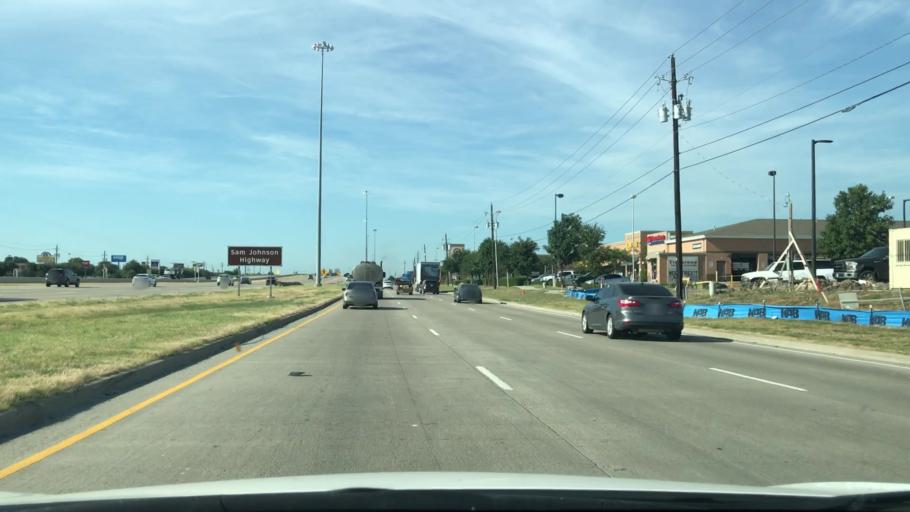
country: US
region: Texas
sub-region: Collin County
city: McKinney
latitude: 33.2226
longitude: -96.6352
